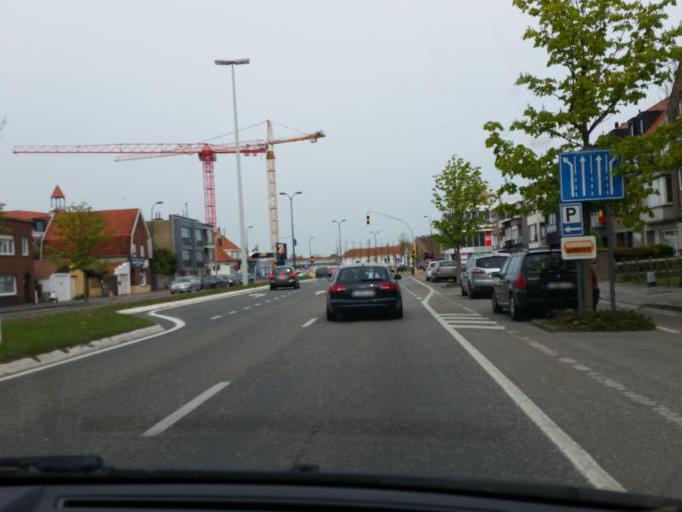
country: BE
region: Flanders
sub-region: Provincie West-Vlaanderen
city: Knokke-Heist
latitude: 51.3372
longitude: 3.2880
